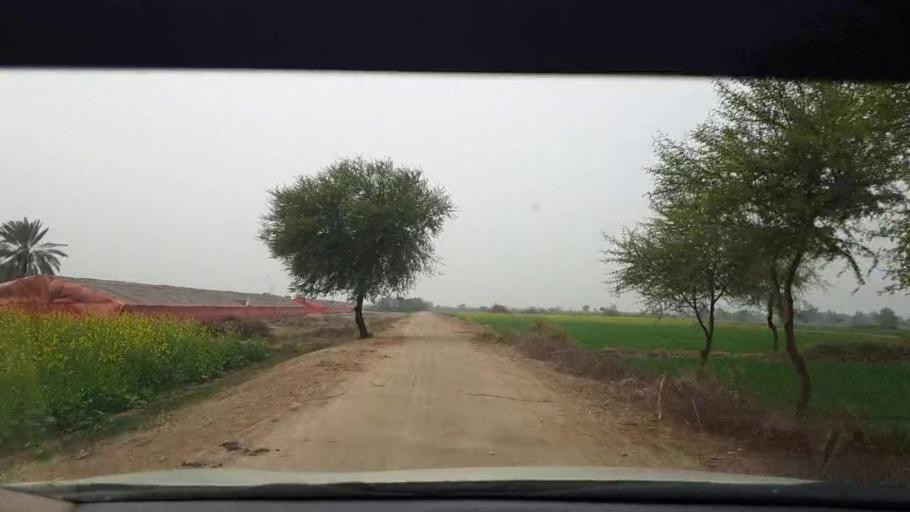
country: PK
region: Sindh
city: Berani
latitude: 25.8287
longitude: 68.8434
